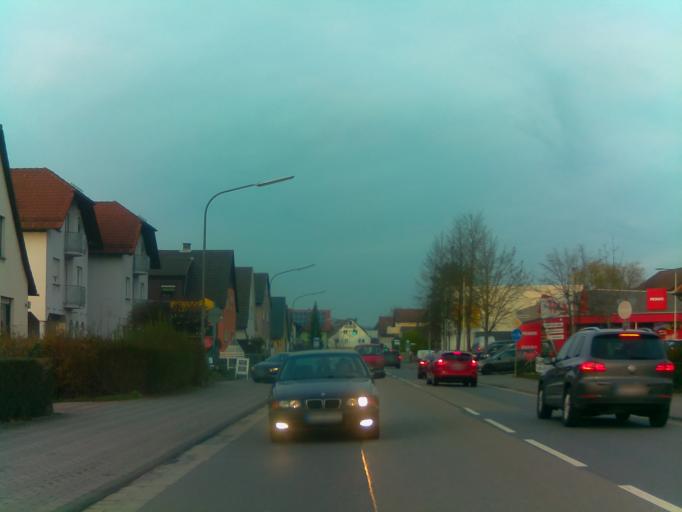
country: DE
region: Hesse
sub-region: Regierungsbezirk Darmstadt
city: Rimbach
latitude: 49.6179
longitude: 8.7576
